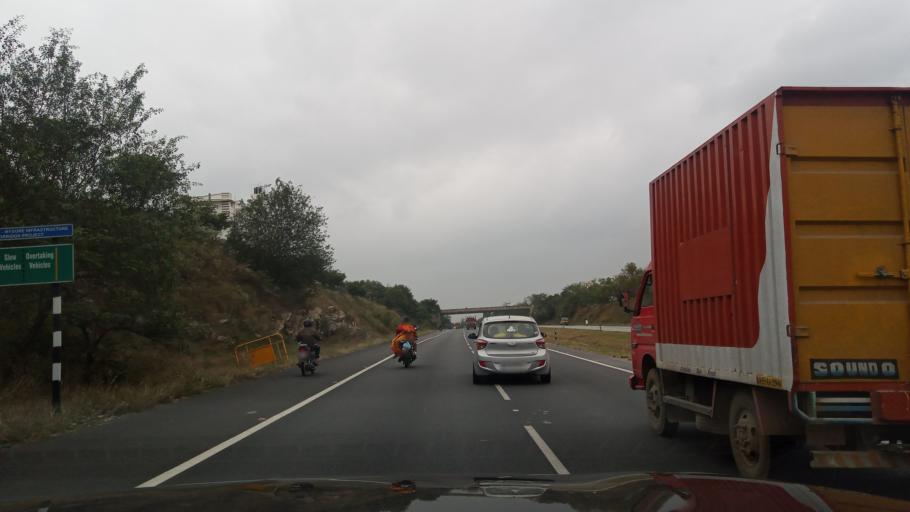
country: IN
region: Karnataka
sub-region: Bangalore Rural
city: Nelamangala
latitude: 13.0119
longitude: 77.4757
